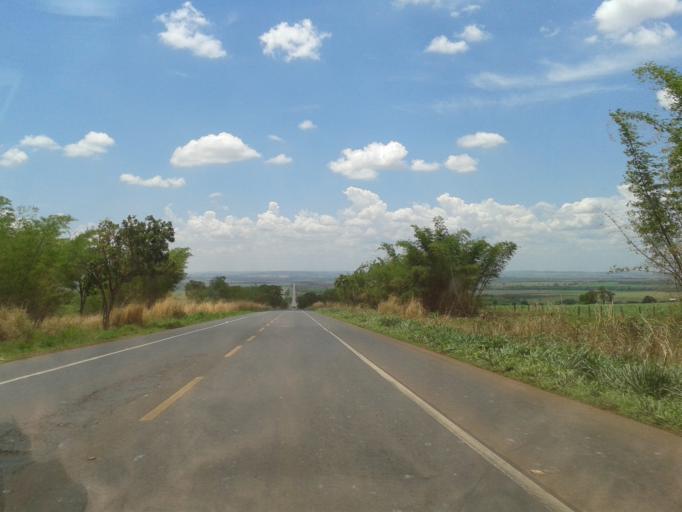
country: BR
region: Goias
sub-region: Goiatuba
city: Goiatuba
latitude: -18.2562
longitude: -49.6758
